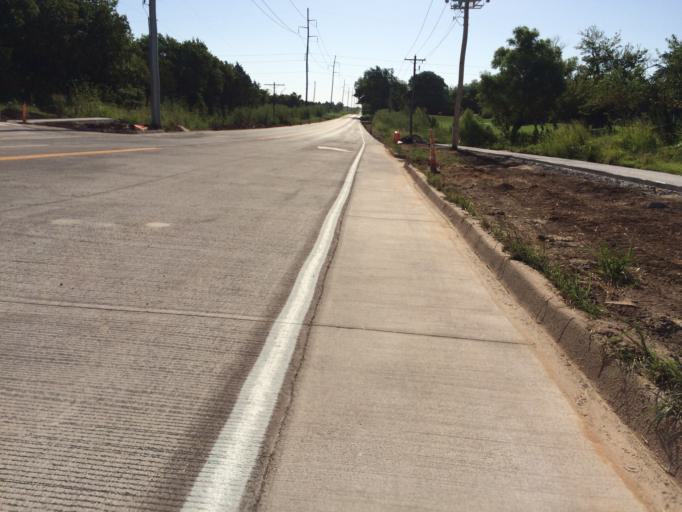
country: US
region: Oklahoma
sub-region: Cleveland County
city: Noble
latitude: 35.1751
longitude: -97.3992
